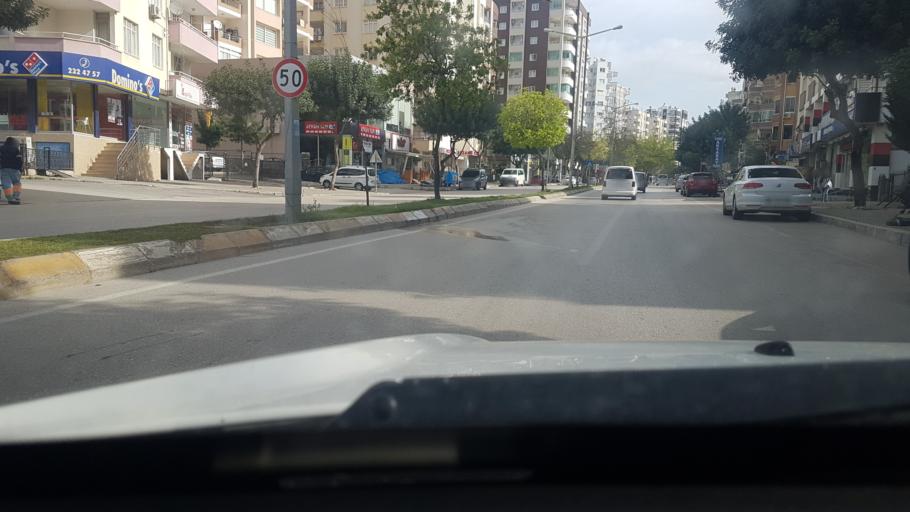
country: TR
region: Adana
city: Adana
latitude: 37.0363
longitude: 35.2985
